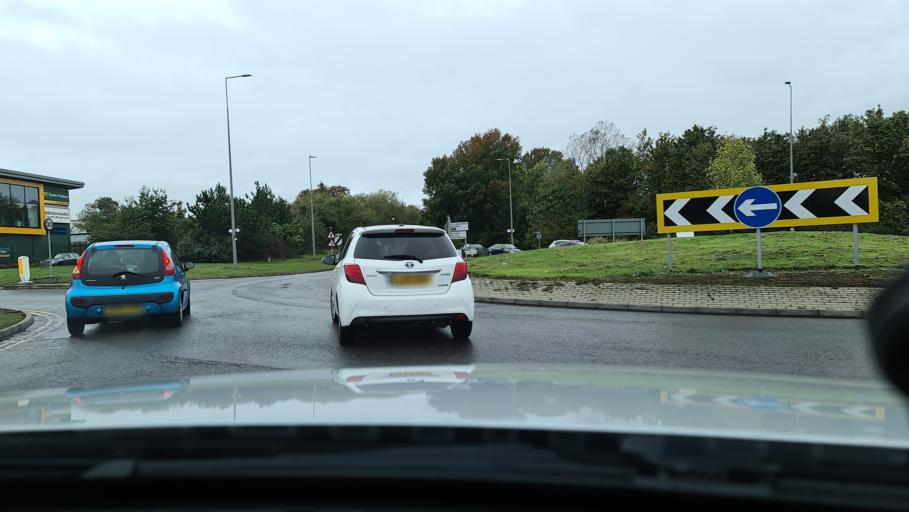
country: GB
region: England
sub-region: Buckinghamshire
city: Bletchley
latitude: 52.0065
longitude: -0.7352
